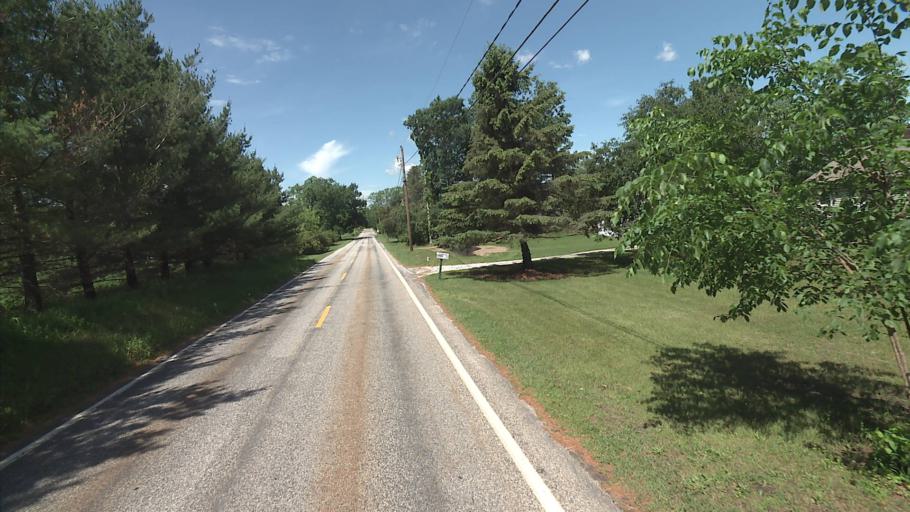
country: US
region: Connecticut
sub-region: Litchfield County
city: Canaan
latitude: 42.0471
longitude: -73.3061
